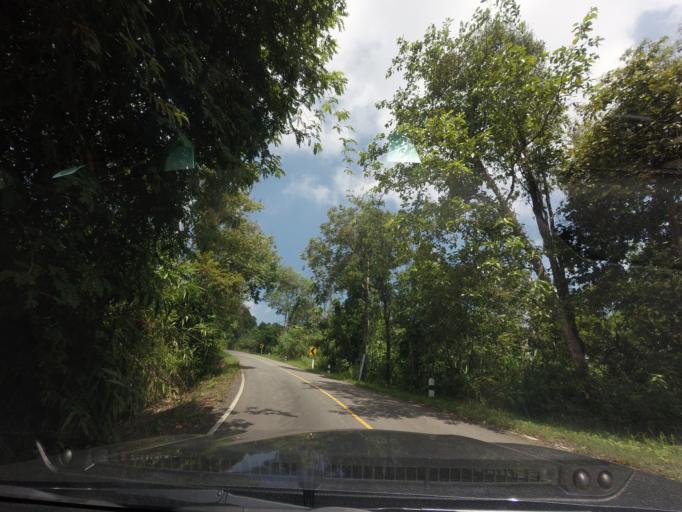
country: TH
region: Loei
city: Na Haeo
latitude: 17.4811
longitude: 100.9152
